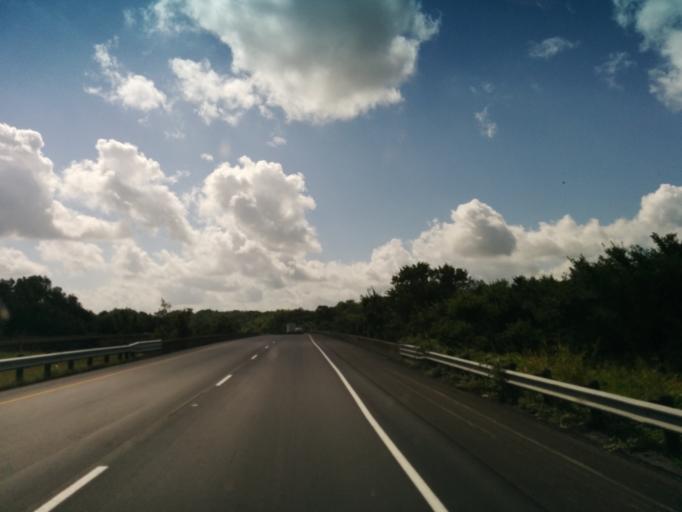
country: US
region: Texas
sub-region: Colorado County
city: Weimar
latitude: 29.6891
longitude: -96.8363
